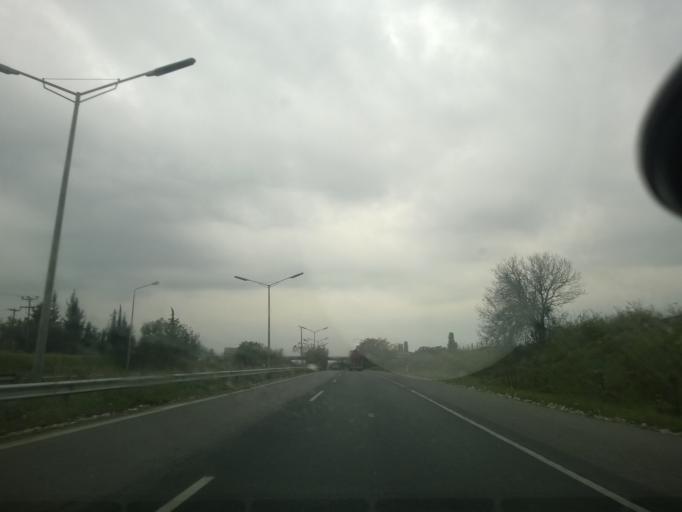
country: GR
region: Central Macedonia
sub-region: Nomos Thessalonikis
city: Agios Athanasios
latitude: 40.7209
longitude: 22.7286
